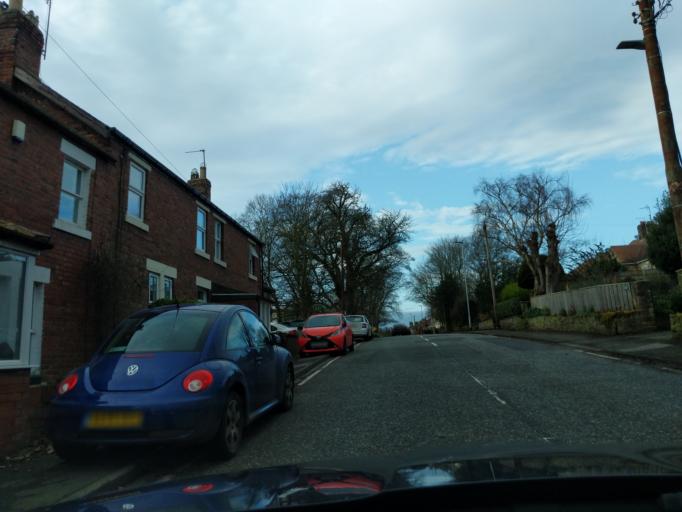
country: GB
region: England
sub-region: Northumberland
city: Ponteland
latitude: 55.0499
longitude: -1.7505
